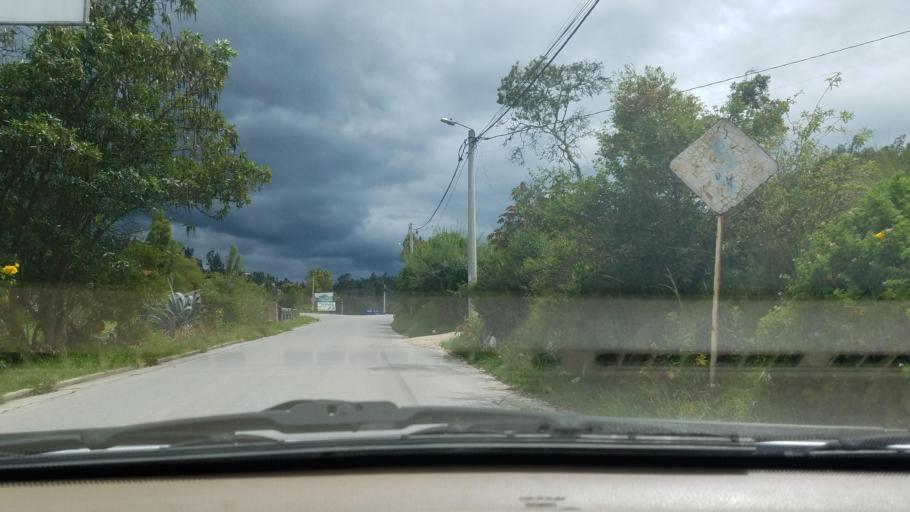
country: CO
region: Boyaca
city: Paipa
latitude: 5.7558
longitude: -73.1072
